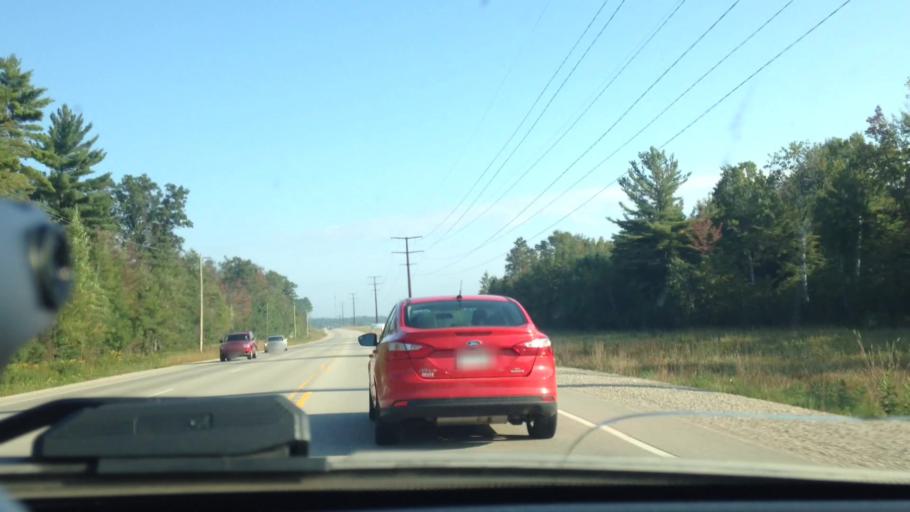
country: US
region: Wisconsin
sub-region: Marinette County
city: Peshtigo
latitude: 45.1934
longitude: -87.9947
